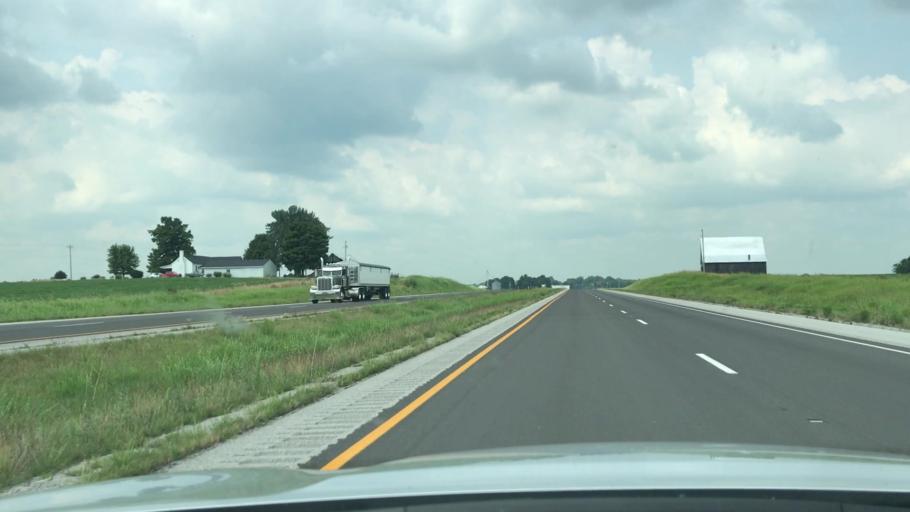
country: US
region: Kentucky
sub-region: Todd County
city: Elkton
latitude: 36.8092
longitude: -87.0436
